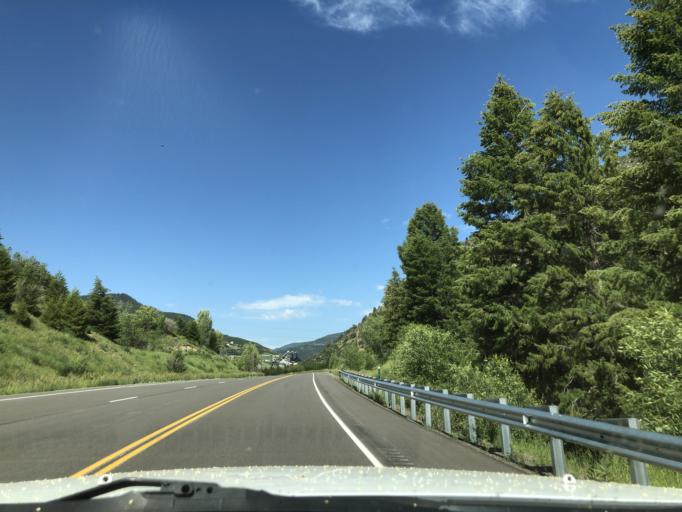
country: US
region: Colorado
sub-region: Delta County
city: Paonia
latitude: 38.9280
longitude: -107.4238
